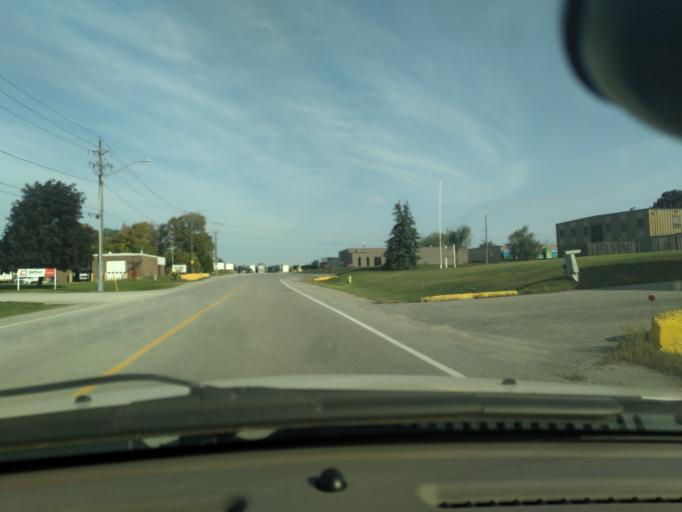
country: CA
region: Ontario
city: Barrie
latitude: 44.3562
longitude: -79.6733
